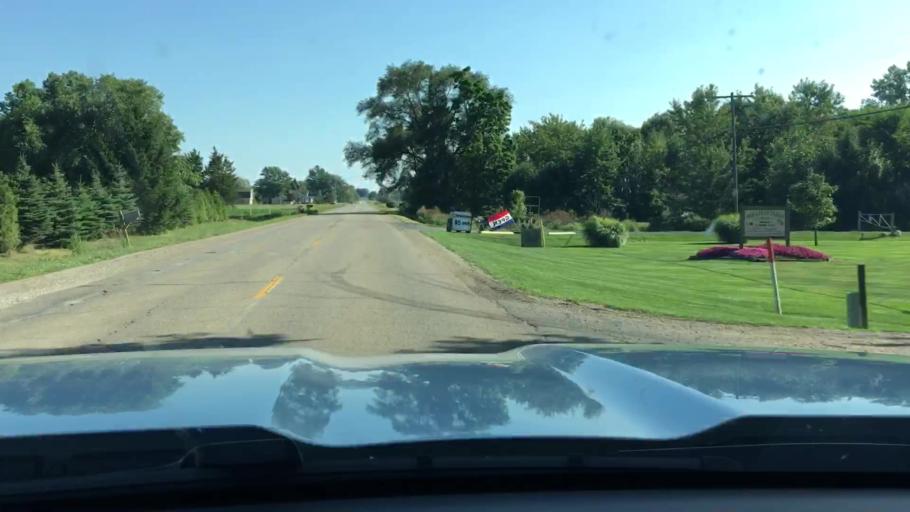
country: US
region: Michigan
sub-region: Ottawa County
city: Zeeland
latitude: 42.8708
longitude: -85.9604
